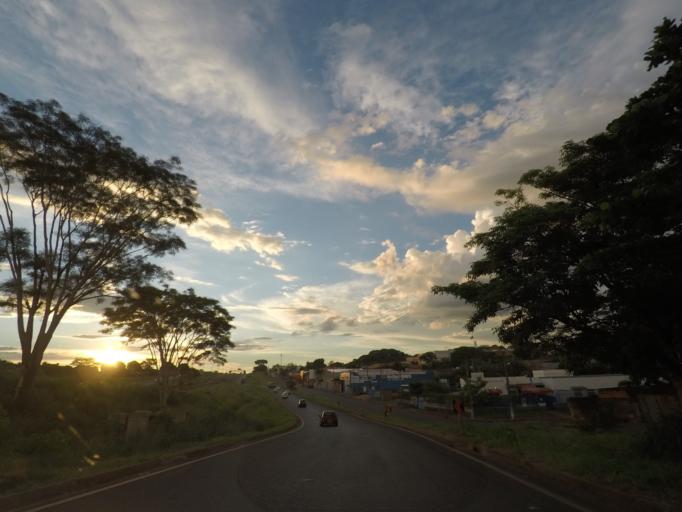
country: BR
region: Minas Gerais
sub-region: Uberaba
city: Uberaba
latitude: -19.7782
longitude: -47.9329
